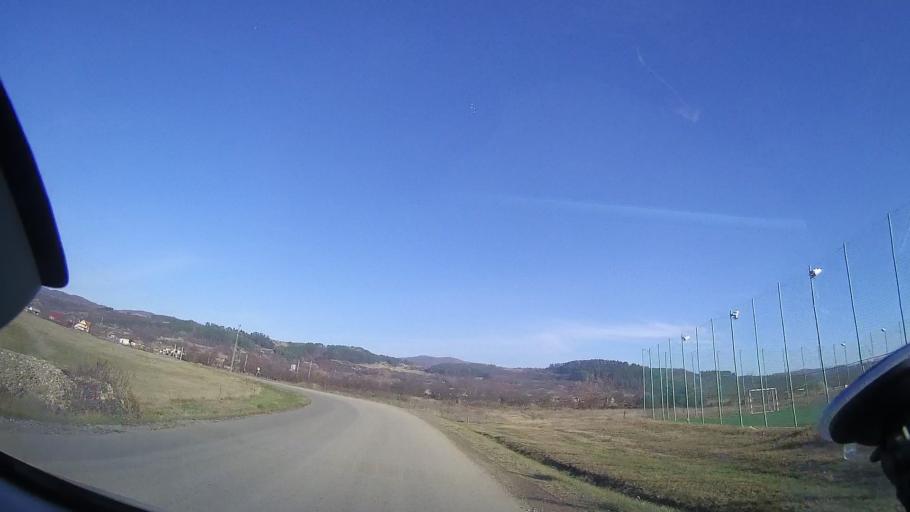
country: RO
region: Bihor
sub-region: Comuna Auseu
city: Auseu
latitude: 47.0286
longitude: 22.4921
